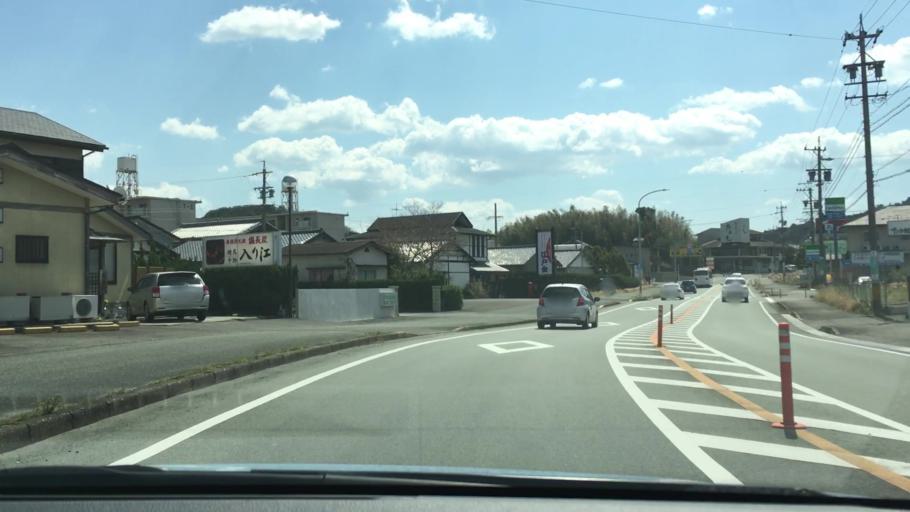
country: JP
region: Mie
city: Toba
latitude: 34.4675
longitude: 136.8534
